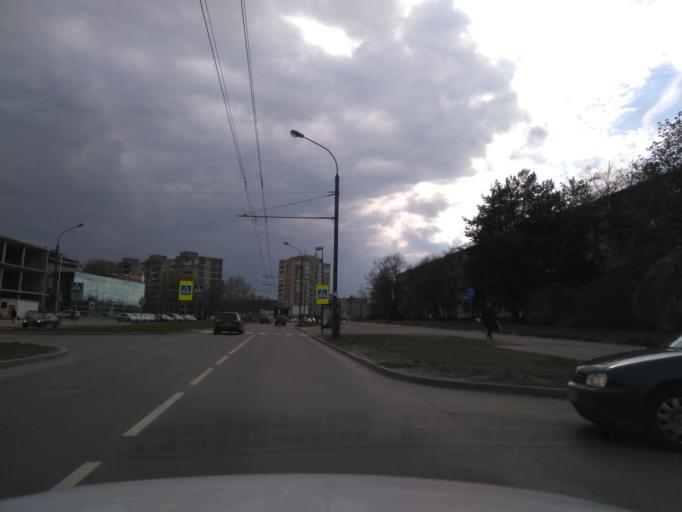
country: LT
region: Kauno apskritis
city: Dainava (Kaunas)
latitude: 54.9169
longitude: 23.9662
